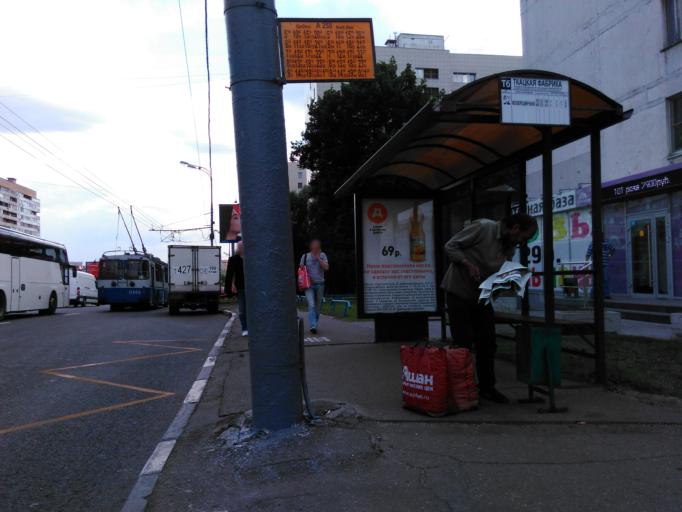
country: RU
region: Moscow
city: Kotlovka
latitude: 55.6695
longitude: 37.5863
